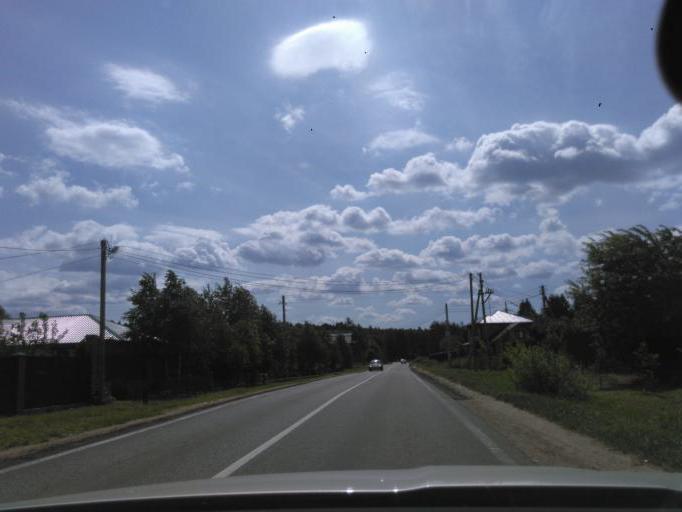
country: RU
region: Moskovskaya
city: Solnechnogorsk
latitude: 56.1591
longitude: 36.9791
